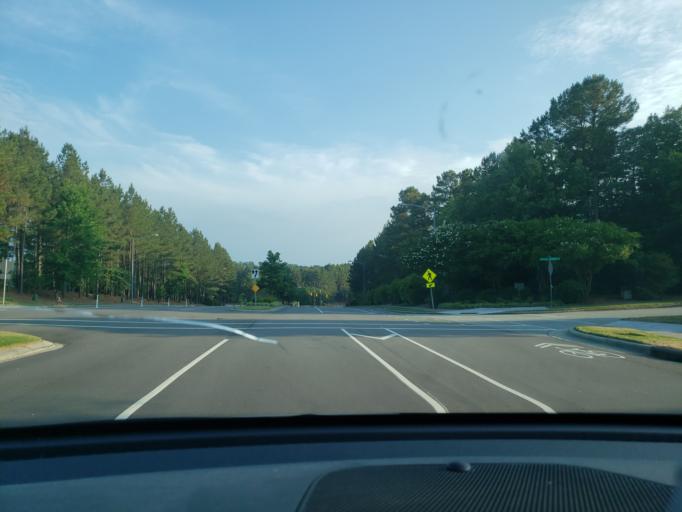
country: US
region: North Carolina
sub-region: Durham County
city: Durham
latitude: 35.9408
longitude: -78.9285
